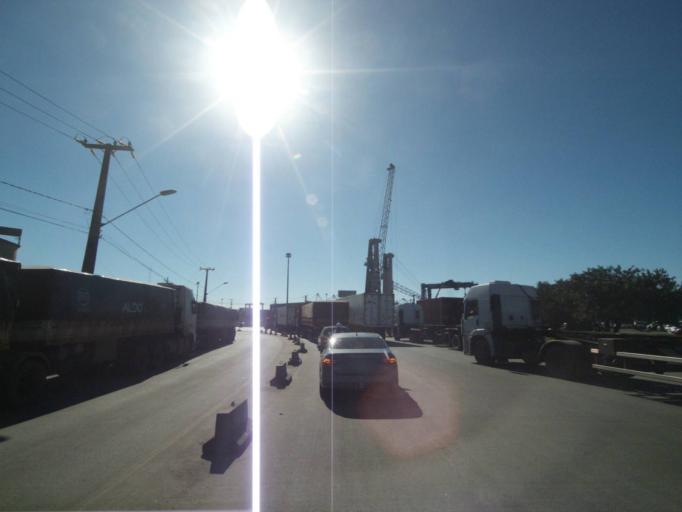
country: BR
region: Parana
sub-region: Paranagua
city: Paranagua
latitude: -25.5068
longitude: -48.5045
